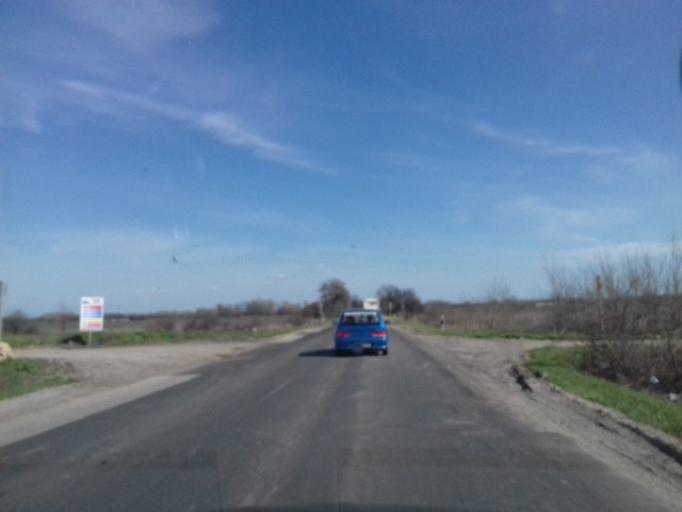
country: HU
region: Jasz-Nagykun-Szolnok
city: Cserkeszolo
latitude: 46.8772
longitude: 20.1522
